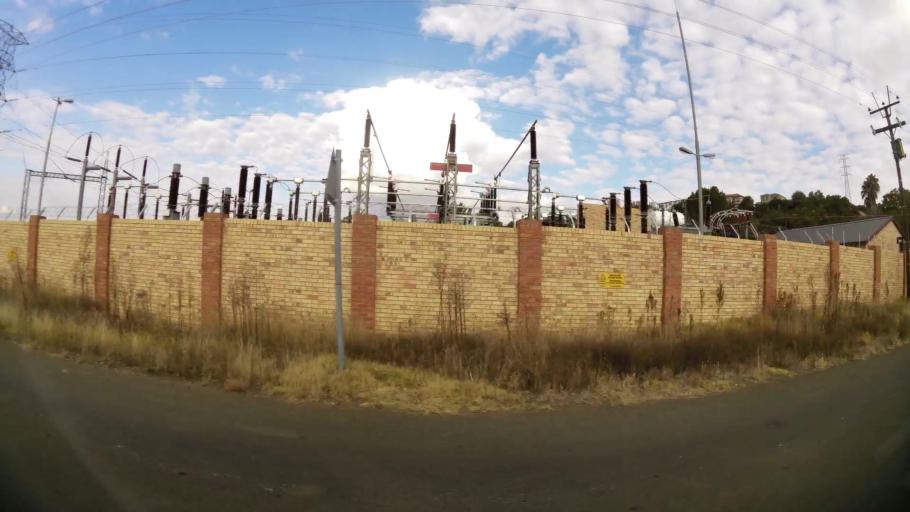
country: ZA
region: Orange Free State
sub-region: Mangaung Metropolitan Municipality
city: Bloemfontein
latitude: -29.0708
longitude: 26.1962
